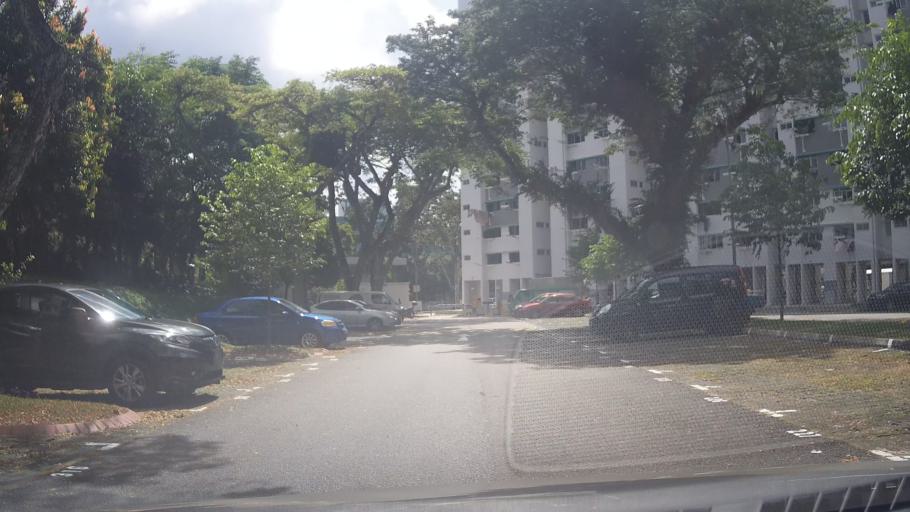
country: MY
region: Johor
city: Johor Bahru
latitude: 1.4470
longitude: 103.7730
